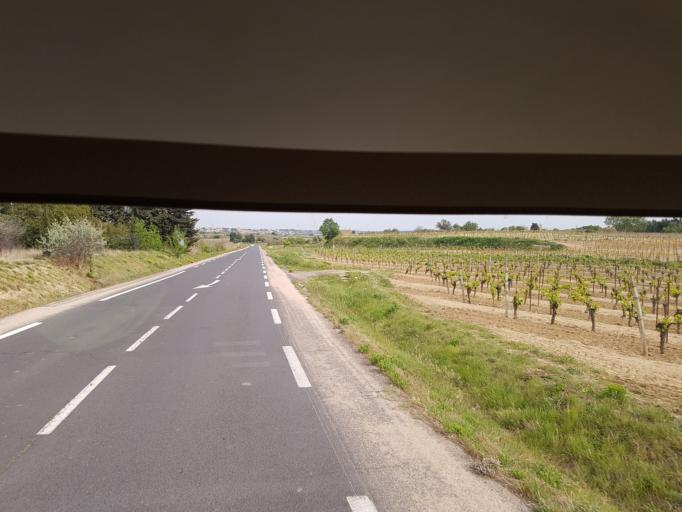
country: FR
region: Languedoc-Roussillon
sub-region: Departement de l'Herault
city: Lespignan
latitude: 43.2772
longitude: 3.1874
